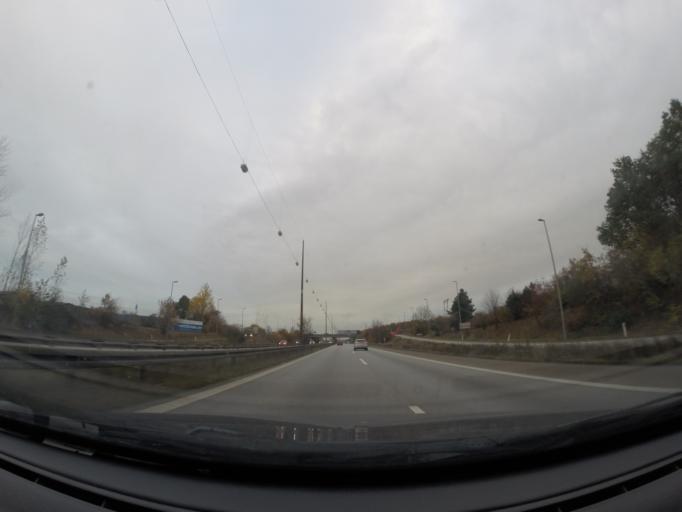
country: DK
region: Capital Region
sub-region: Ishoj Kommune
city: Ishoj
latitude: 55.6200
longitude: 12.3274
